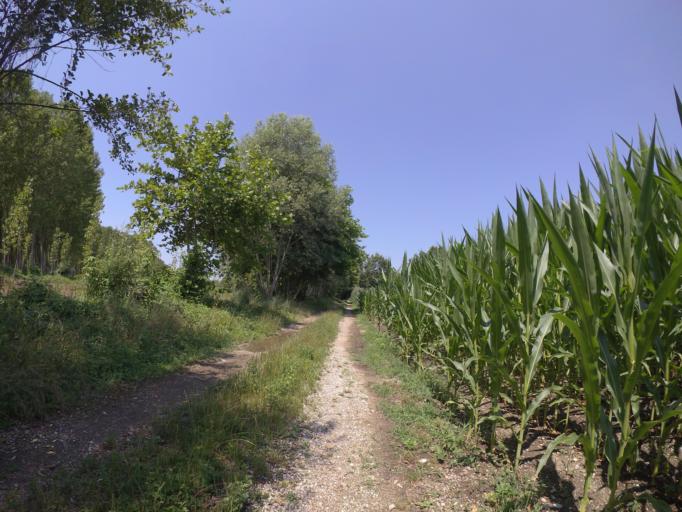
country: IT
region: Friuli Venezia Giulia
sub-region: Provincia di Udine
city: Rivignano
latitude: 45.9038
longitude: 13.0410
